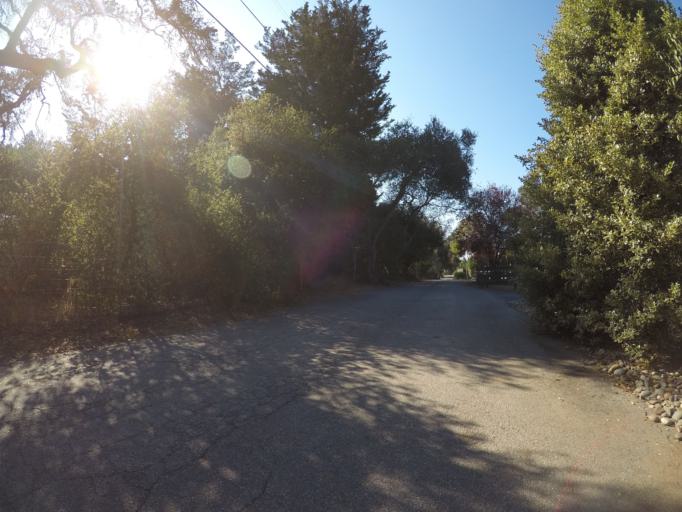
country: US
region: California
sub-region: Santa Cruz County
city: Scotts Valley
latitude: 37.0428
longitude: -122.0165
